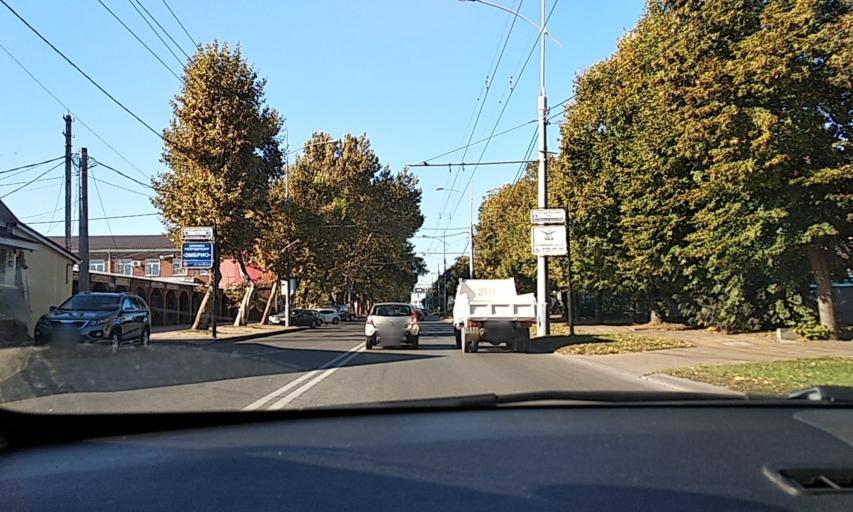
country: RU
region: Krasnodarskiy
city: Pashkovskiy
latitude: 45.0180
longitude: 39.0995
